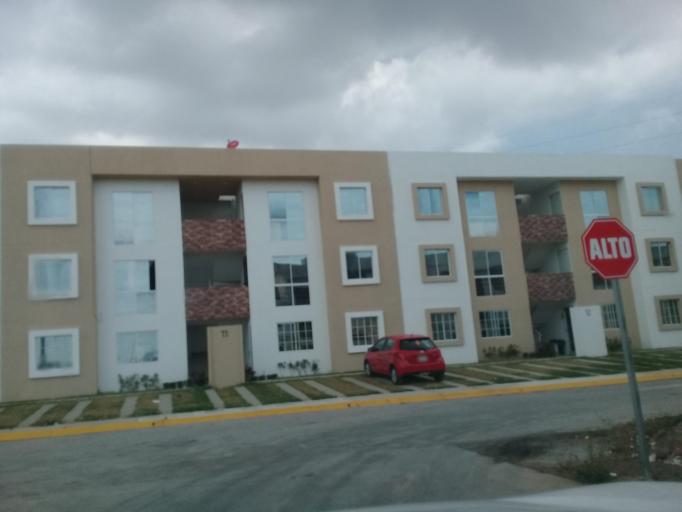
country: MX
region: Veracruz
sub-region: Veracruz
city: Las Amapolas
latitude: 19.1430
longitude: -96.2356
